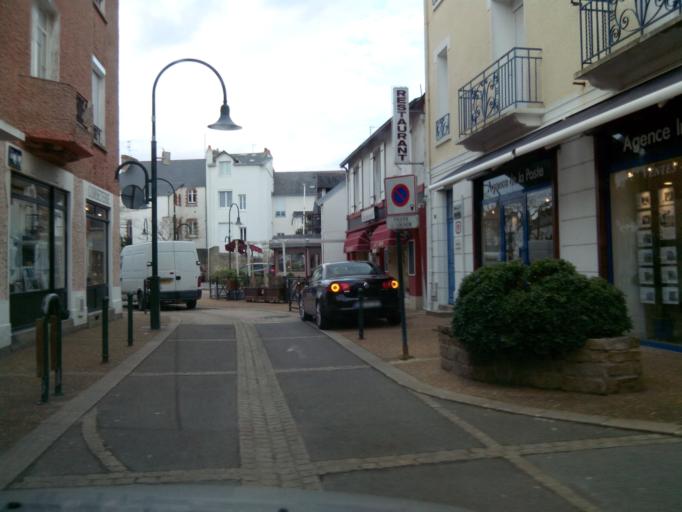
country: FR
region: Pays de la Loire
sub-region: Departement de la Loire-Atlantique
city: Le Pouliguen
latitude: 47.2777
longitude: -2.4299
